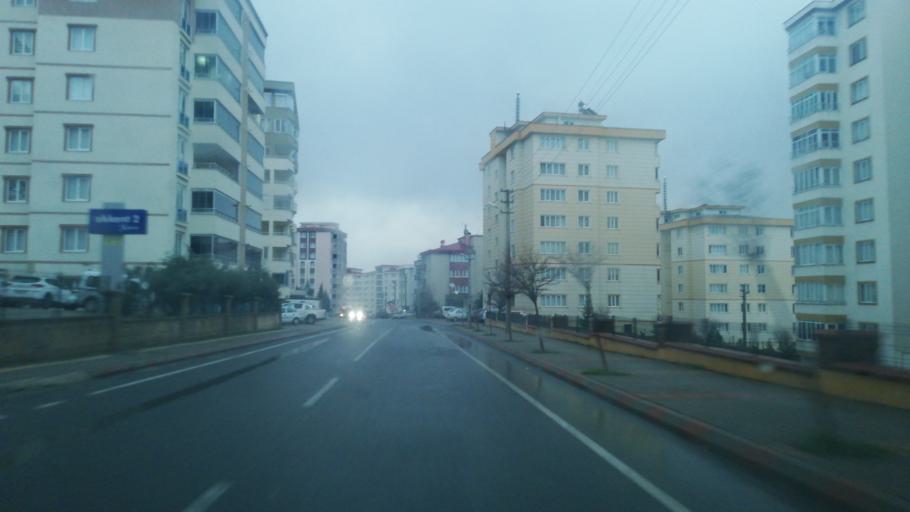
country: TR
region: Kahramanmaras
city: Kahramanmaras
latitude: 37.5995
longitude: 36.8860
